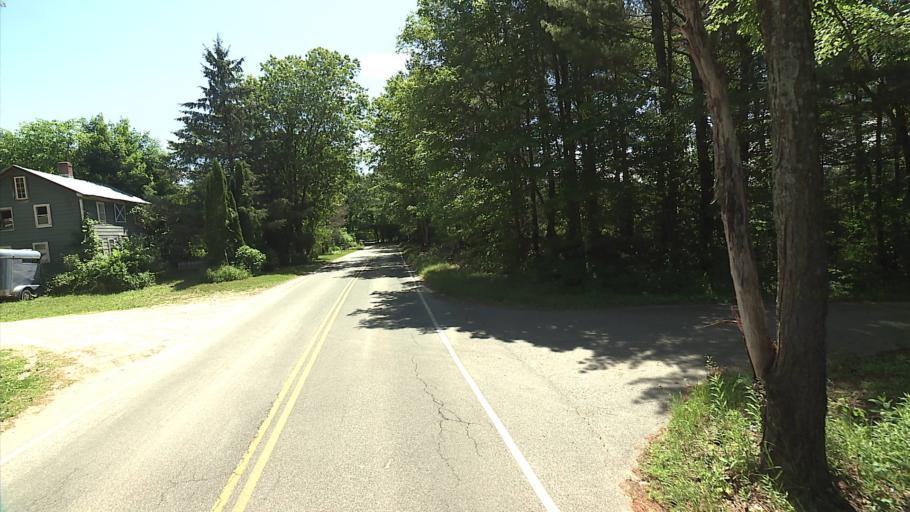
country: US
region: Connecticut
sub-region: Litchfield County
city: Canaan
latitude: 42.0469
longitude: -73.2948
